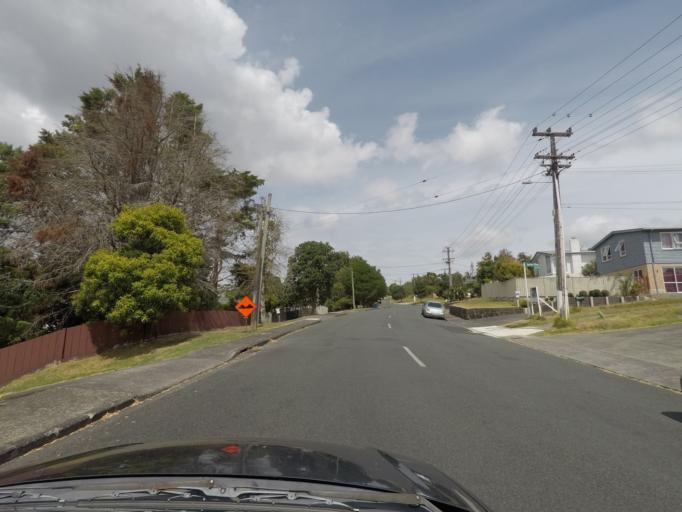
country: NZ
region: Auckland
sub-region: Auckland
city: Waitakere
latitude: -36.8973
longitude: 174.6372
